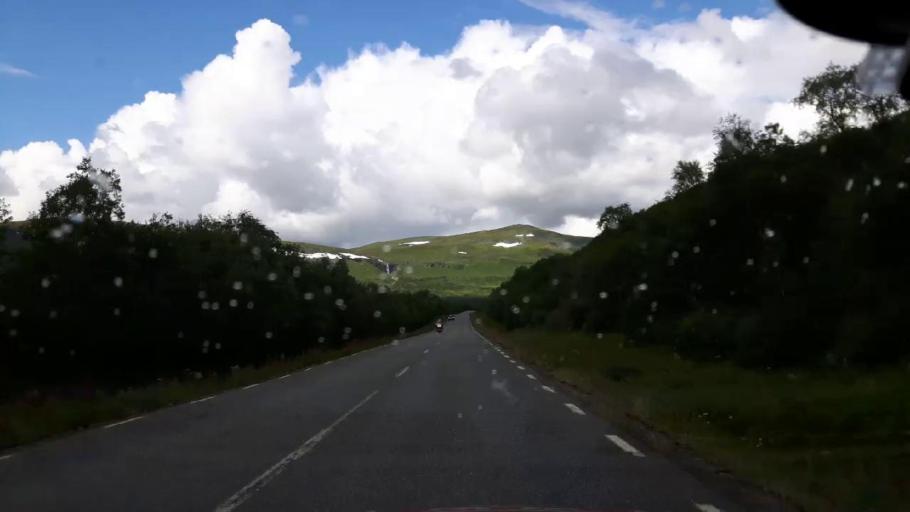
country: NO
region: Nordland
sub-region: Hattfjelldal
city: Hattfjelldal
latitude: 65.0681
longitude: 14.6760
